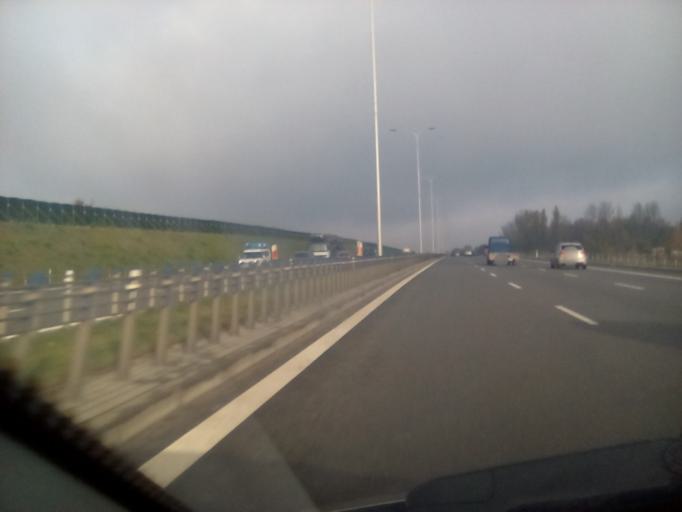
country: PL
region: Masovian Voivodeship
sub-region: Powiat pruszkowski
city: Rybie
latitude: 52.1473
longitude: 20.9634
